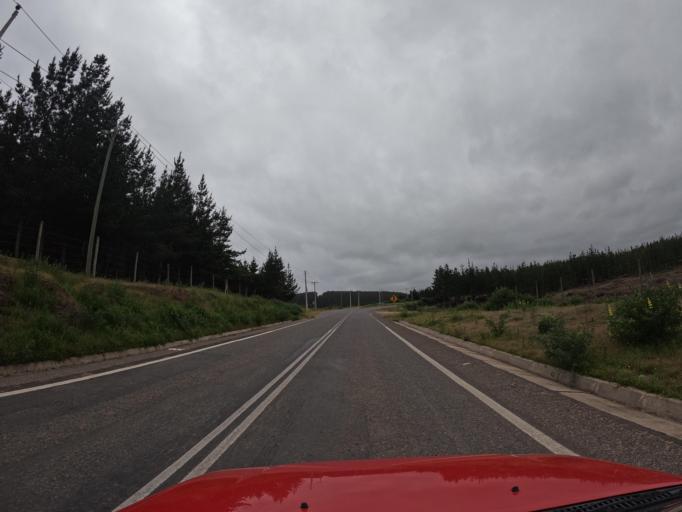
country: CL
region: O'Higgins
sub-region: Provincia de Colchagua
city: Santa Cruz
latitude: -34.6369
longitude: -72.0356
